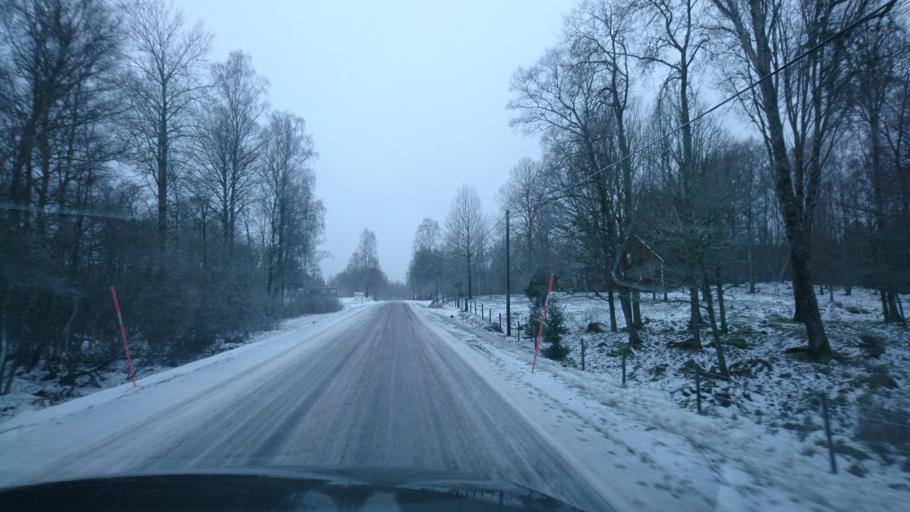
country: SE
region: Vaestra Goetaland
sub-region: Falkopings Kommun
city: Floby
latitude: 58.0771
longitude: 13.3873
